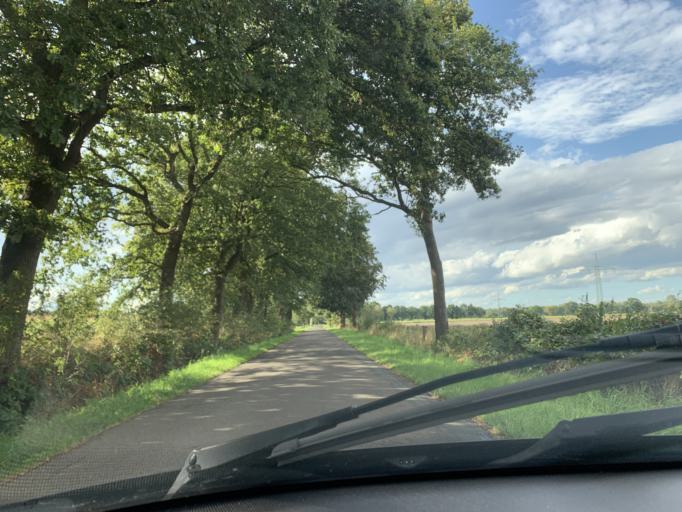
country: DE
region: Lower Saxony
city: Bockhorn
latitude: 53.3129
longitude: 8.0060
